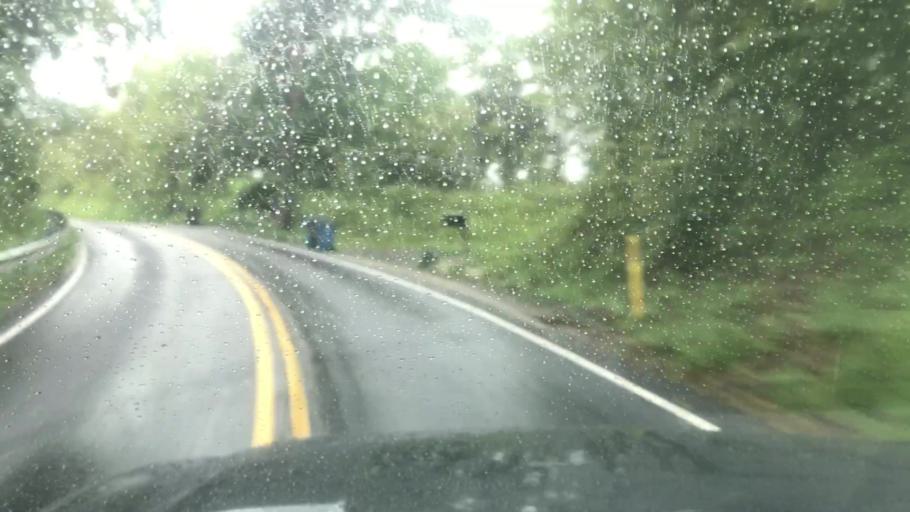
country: US
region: Pennsylvania
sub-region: Cumberland County
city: Shiremanstown
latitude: 40.1757
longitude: -76.9454
